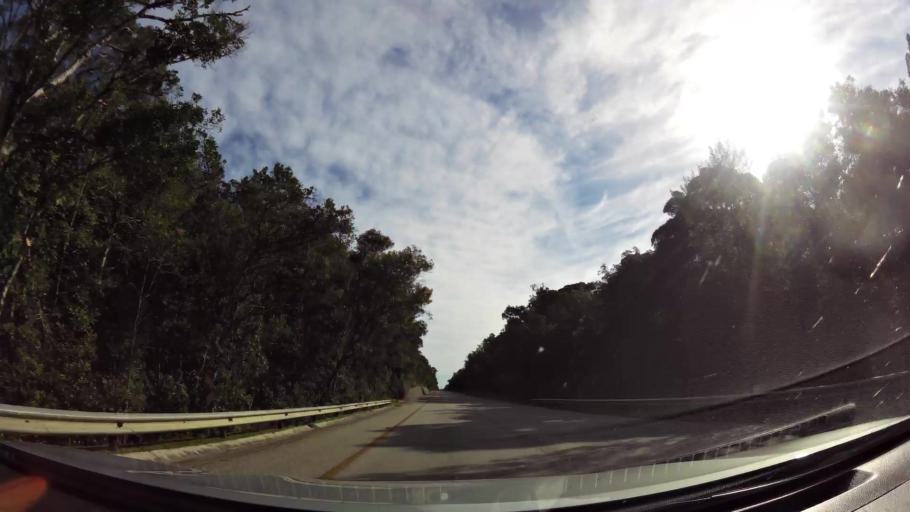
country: ZA
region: Eastern Cape
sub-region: Cacadu District Municipality
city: Kareedouw
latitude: -33.9672
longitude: 23.9068
